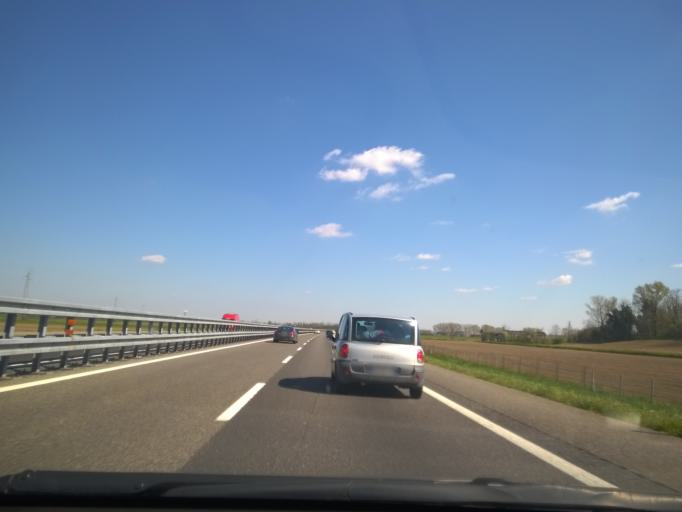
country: IT
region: Emilia-Romagna
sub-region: Provincia di Piacenza
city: Castel San Giovanni
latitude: 45.0790
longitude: 9.4298
